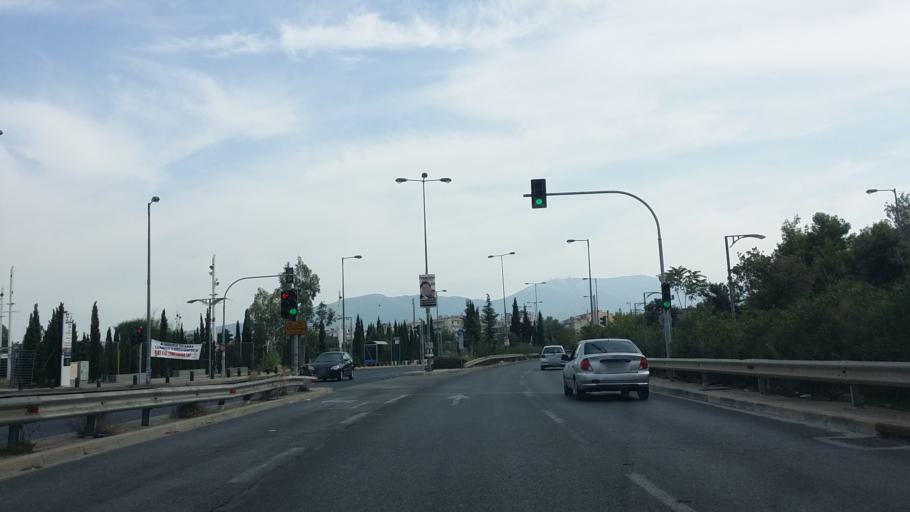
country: GR
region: Attica
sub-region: Nomarchia Athinas
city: Filothei
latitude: 38.0378
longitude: 23.7800
